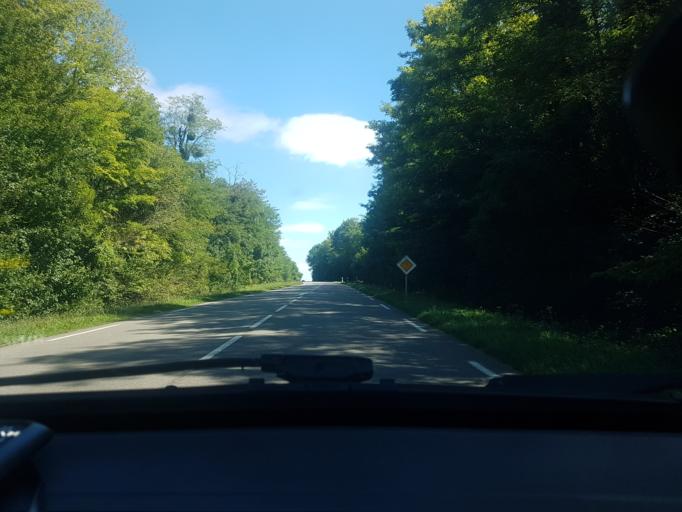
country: FR
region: Bourgogne
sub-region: Departement de la Cote-d'Or
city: Mirebeau-sur-Beze
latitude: 47.4048
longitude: 5.3743
